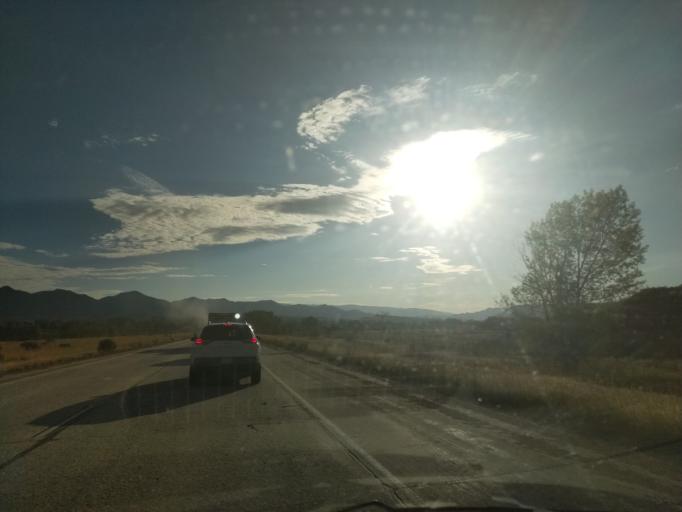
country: US
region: Colorado
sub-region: Garfield County
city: Silt
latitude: 39.5402
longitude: -107.6780
